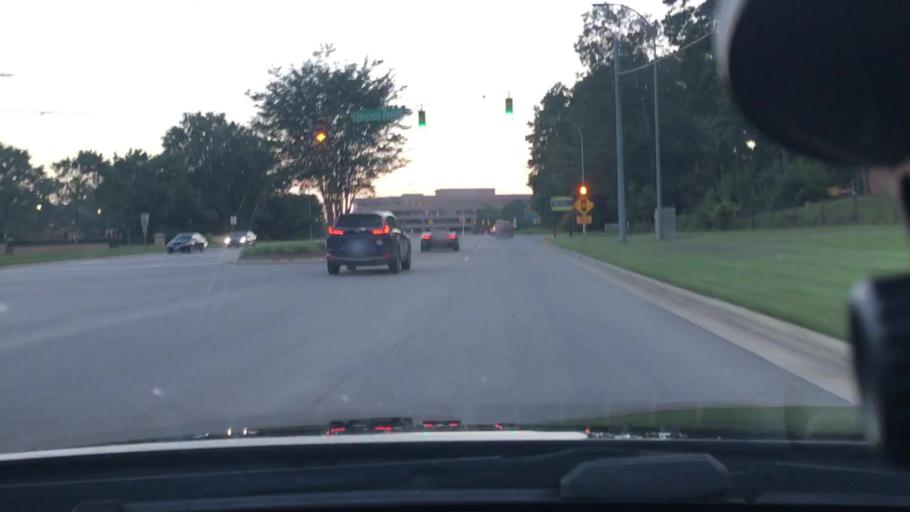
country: US
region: North Carolina
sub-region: Wake County
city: Cary
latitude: 35.7375
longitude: -78.7850
